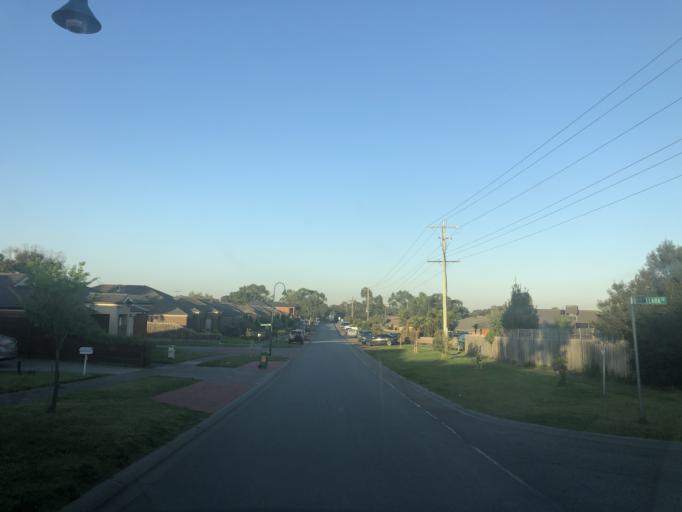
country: AU
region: Victoria
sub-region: Casey
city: Lynbrook
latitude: -38.0460
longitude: 145.2579
